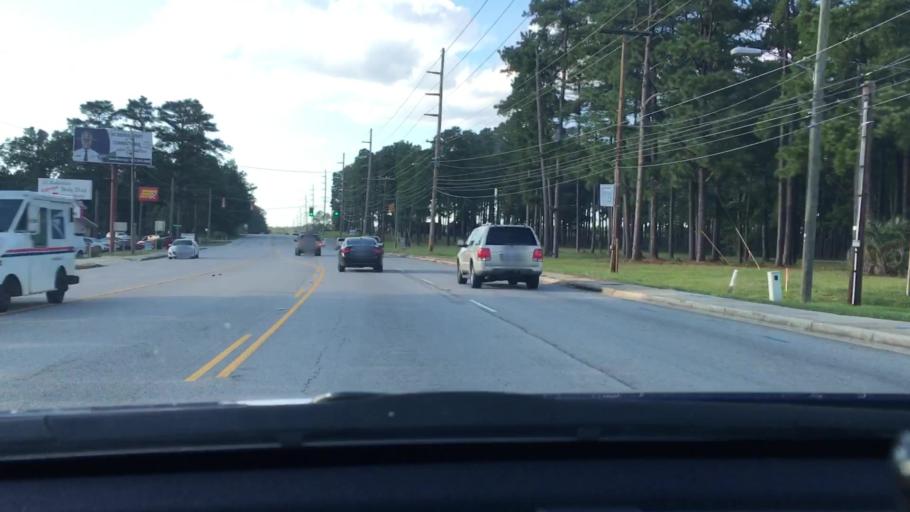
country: US
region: South Carolina
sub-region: Lexington County
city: Saint Andrews
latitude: 34.0700
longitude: -81.1193
